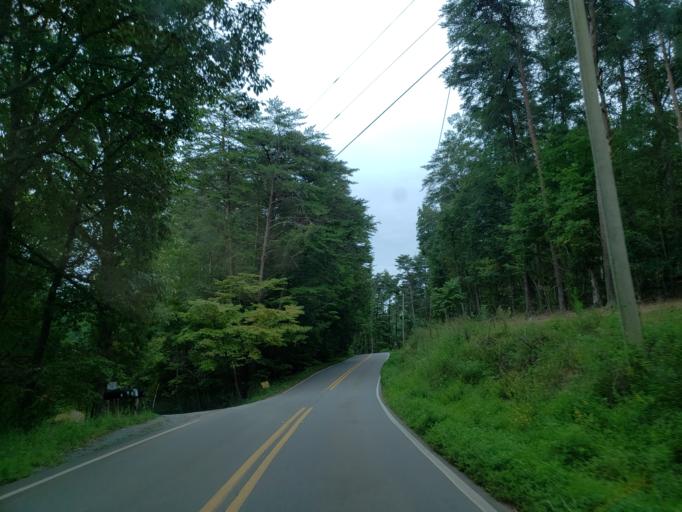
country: US
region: Georgia
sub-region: Pickens County
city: Jasper
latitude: 34.4252
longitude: -84.5438
